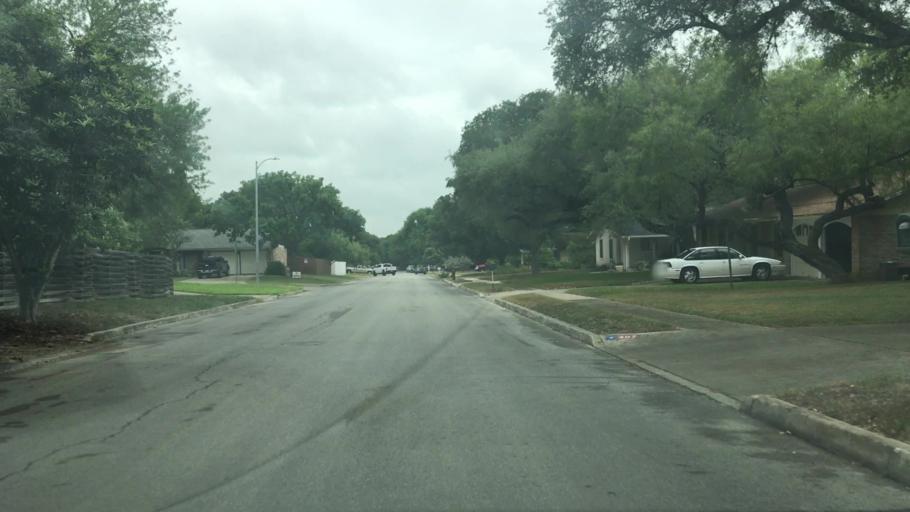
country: US
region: Texas
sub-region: Bexar County
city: Universal City
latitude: 29.5514
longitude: -98.3147
